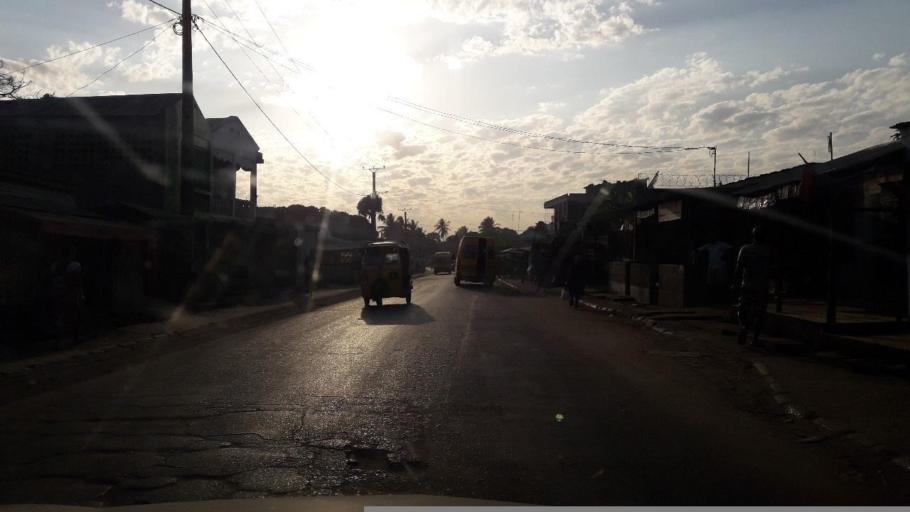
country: MG
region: Boeny
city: Mahajanga
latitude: -15.7167
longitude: 46.3451
